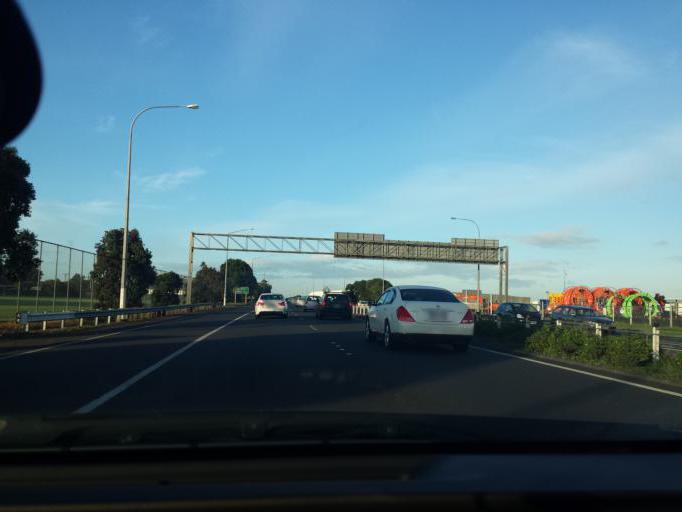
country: NZ
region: Auckland
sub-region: Auckland
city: Mangere
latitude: -36.9742
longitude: 174.7892
